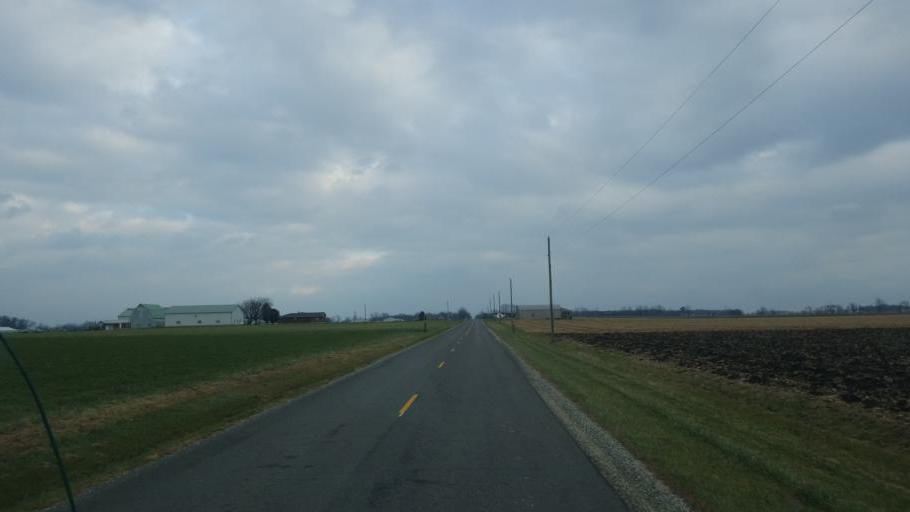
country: US
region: Ohio
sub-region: Mercer County
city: Coldwater
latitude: 40.5089
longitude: -84.6728
